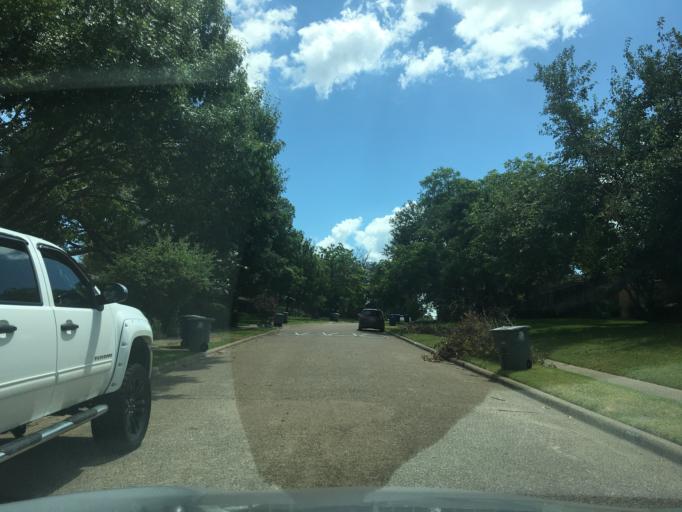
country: US
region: Texas
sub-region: Dallas County
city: Richardson
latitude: 32.8686
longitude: -96.7120
